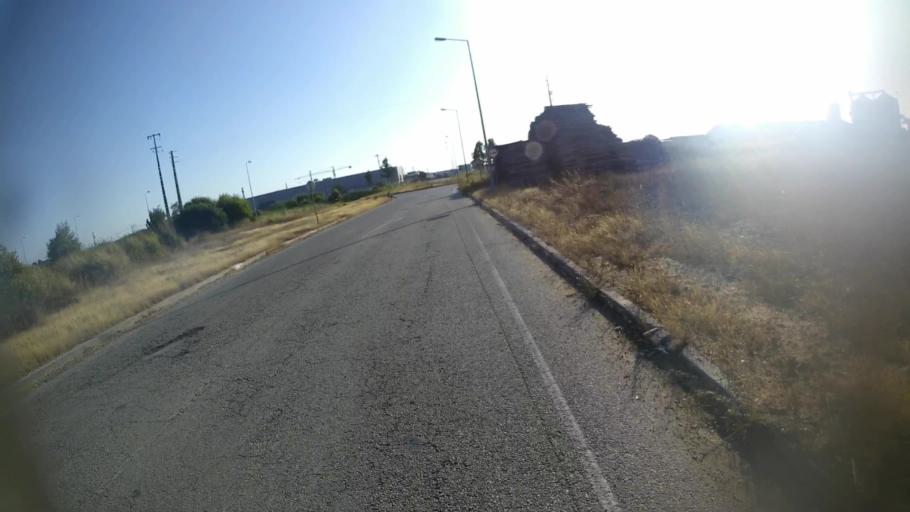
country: PT
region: Aveiro
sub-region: Ilhavo
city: Gafanha da Nazare
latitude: 40.6357
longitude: -8.6814
